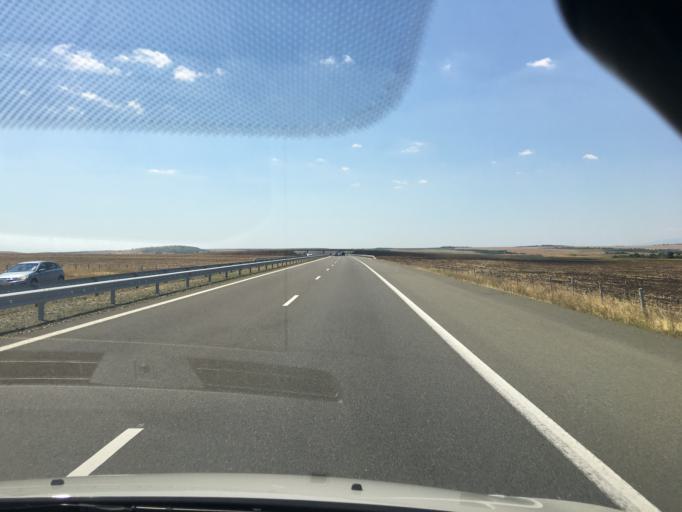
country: BG
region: Burgas
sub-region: Obshtina Karnobat
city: Karnobat
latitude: 42.5852
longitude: 26.9358
